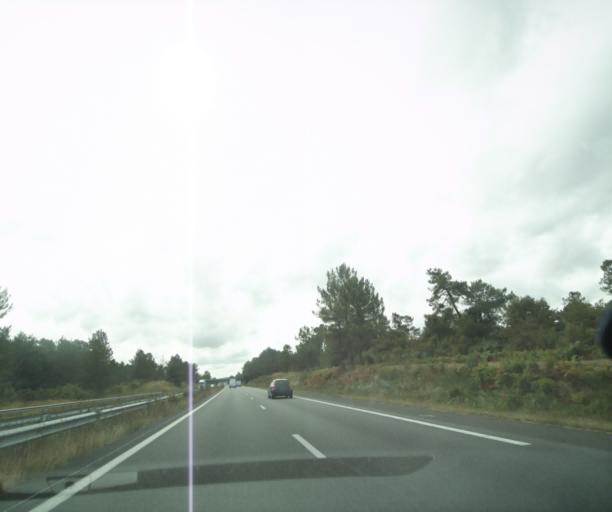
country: FR
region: Poitou-Charentes
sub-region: Departement de la Charente-Maritime
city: Saint-Genis-de-Saintonge
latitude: 45.4572
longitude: -0.6170
